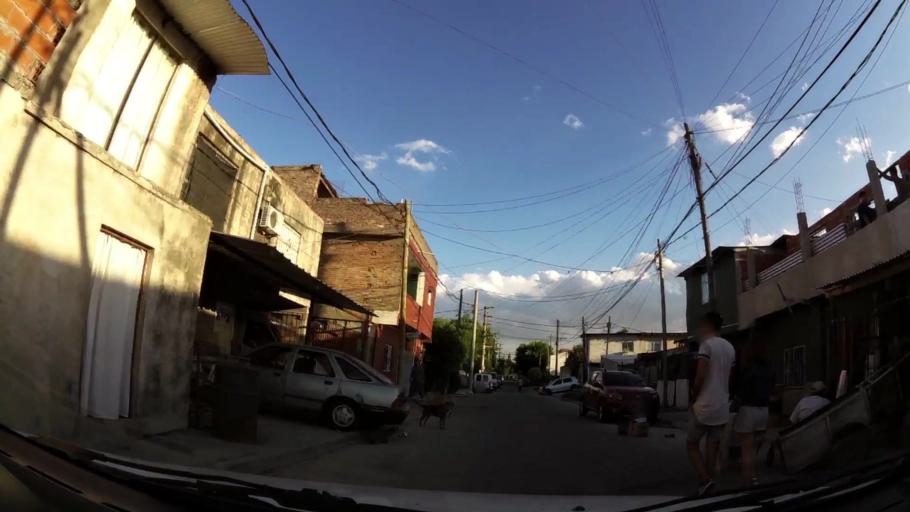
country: AR
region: Buenos Aires
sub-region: Partido de San Isidro
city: San Isidro
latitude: -34.4669
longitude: -58.5514
